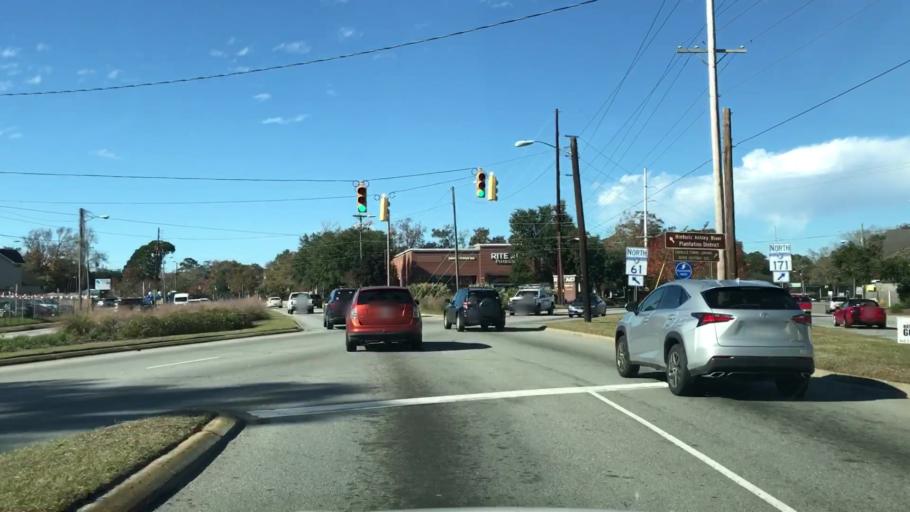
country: US
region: South Carolina
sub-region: Charleston County
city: North Charleston
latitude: 32.7962
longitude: -79.9946
